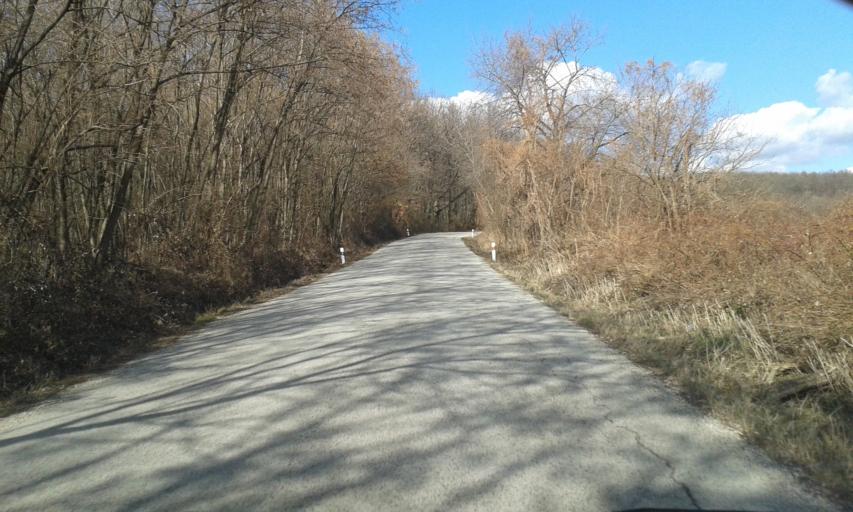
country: SK
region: Nitriansky
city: Zlate Moravce
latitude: 48.4401
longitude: 18.3205
